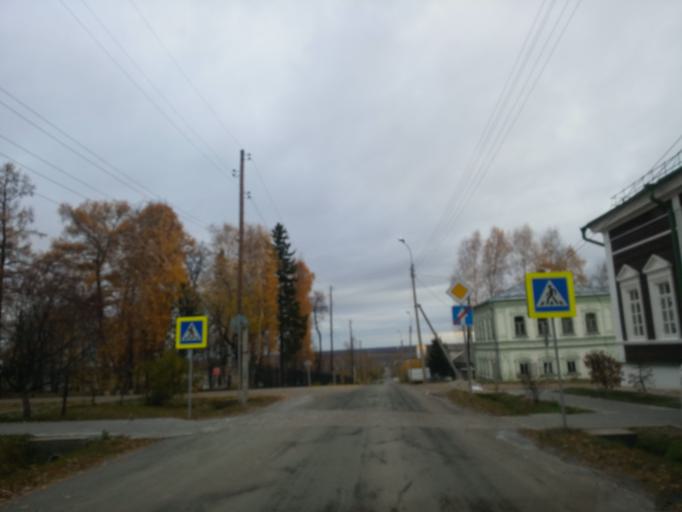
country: RU
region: Sverdlovsk
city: Turinsk
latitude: 58.0584
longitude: 63.6905
